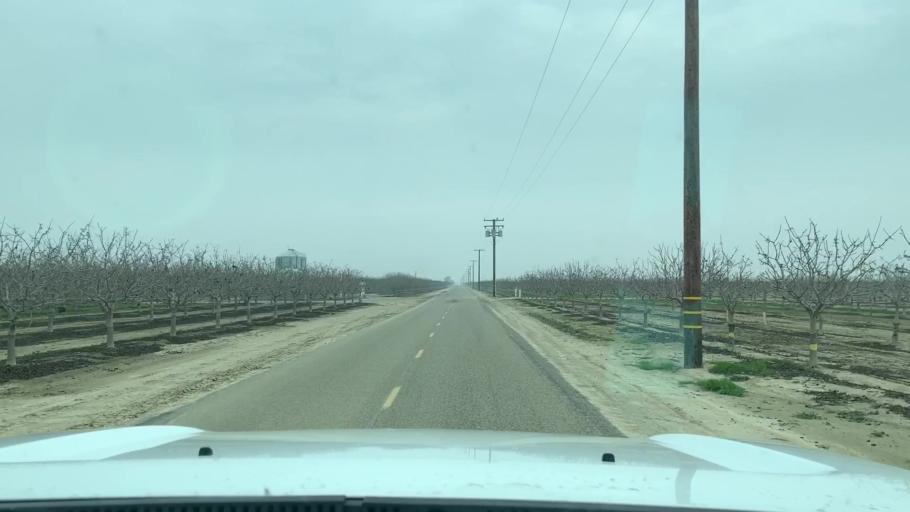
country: US
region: California
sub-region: Tulare County
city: Earlimart
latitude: 35.8193
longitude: -119.3453
